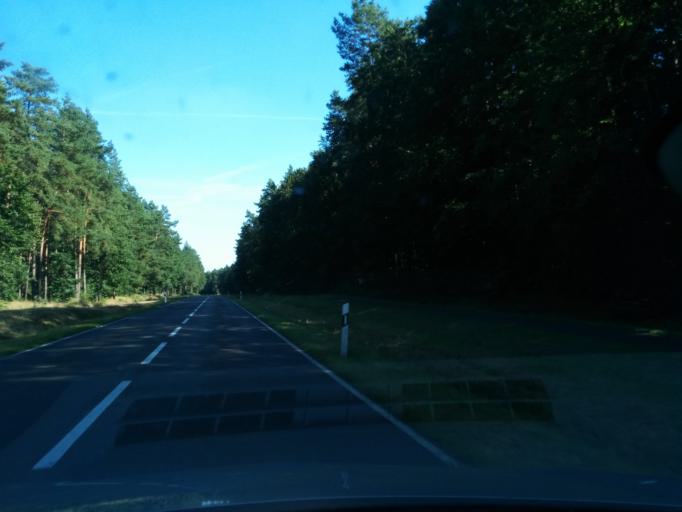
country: DE
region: Mecklenburg-Vorpommern
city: Ferdinandshof
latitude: 53.6406
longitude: 13.9405
